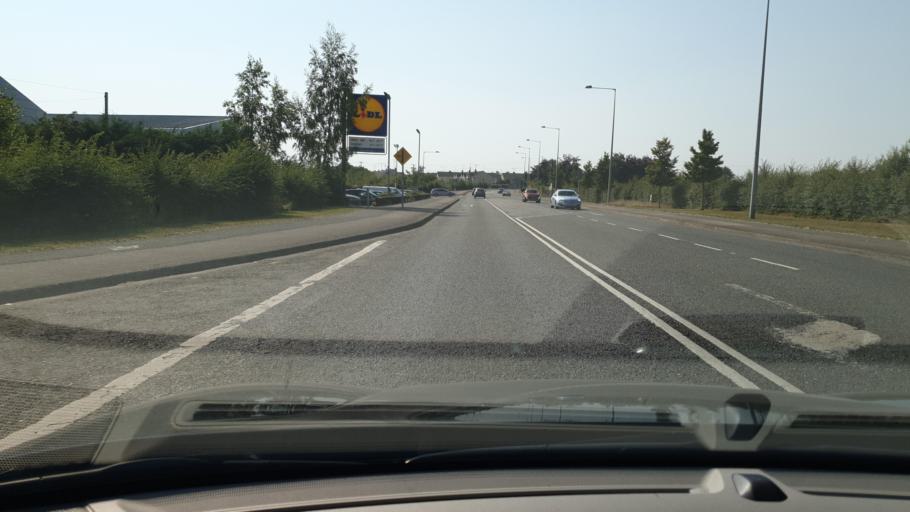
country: IE
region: Leinster
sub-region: An Mhi
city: Trim
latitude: 53.5623
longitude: -6.7904
